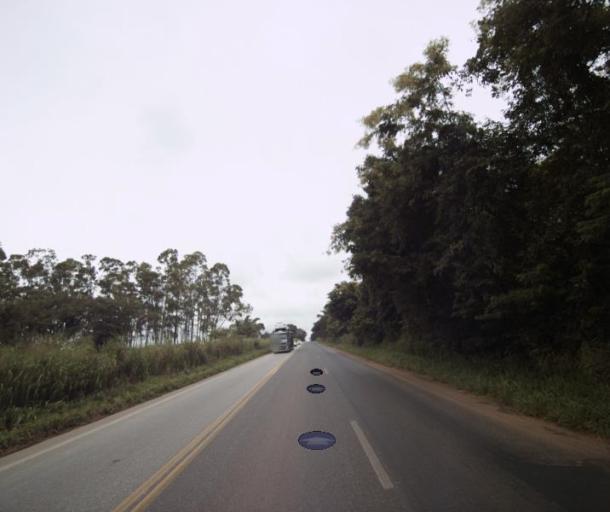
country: BR
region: Goias
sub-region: Uruacu
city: Uruacu
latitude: -14.5938
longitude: -49.1633
